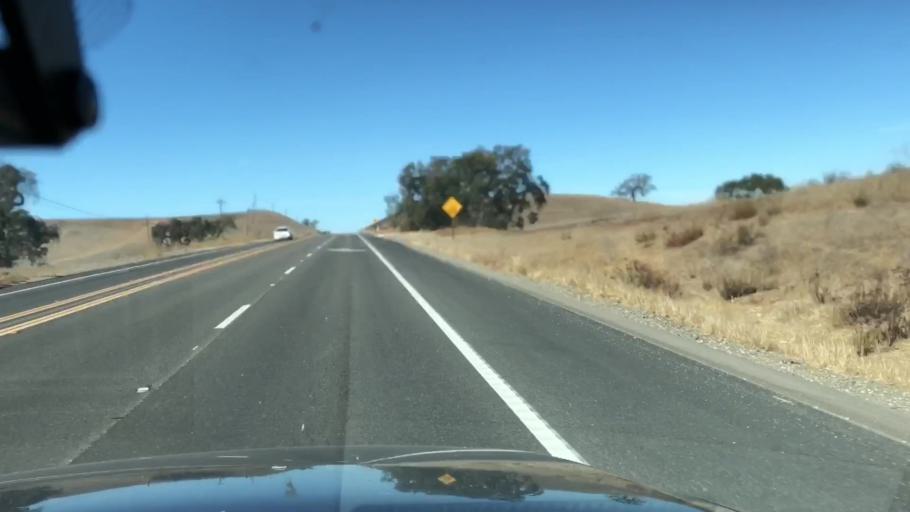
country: US
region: California
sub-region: Santa Barbara County
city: Santa Ynez
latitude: 34.5951
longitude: -120.0381
